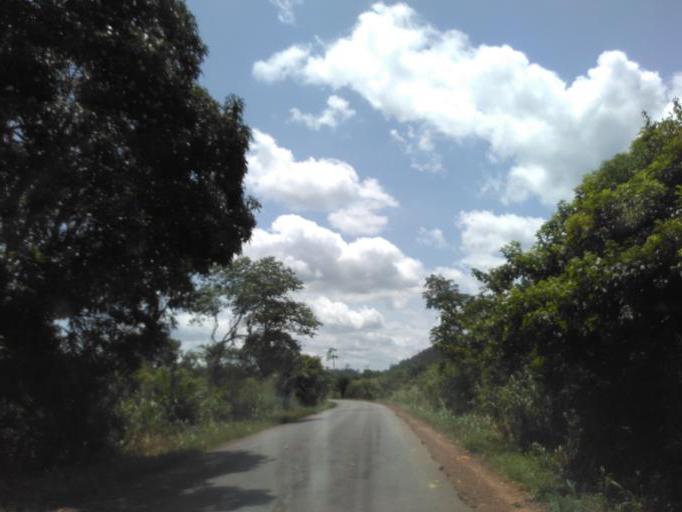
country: GH
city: Akropong
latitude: 6.0483
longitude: -0.0916
